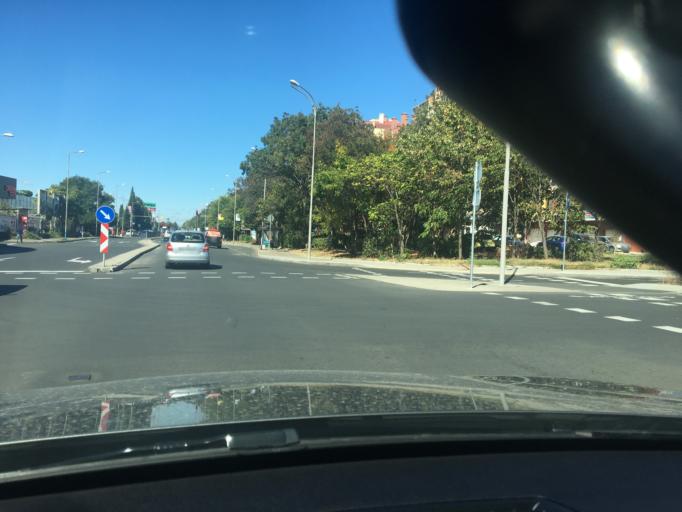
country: BG
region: Burgas
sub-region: Obshtina Burgas
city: Burgas
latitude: 42.5124
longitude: 27.4576
